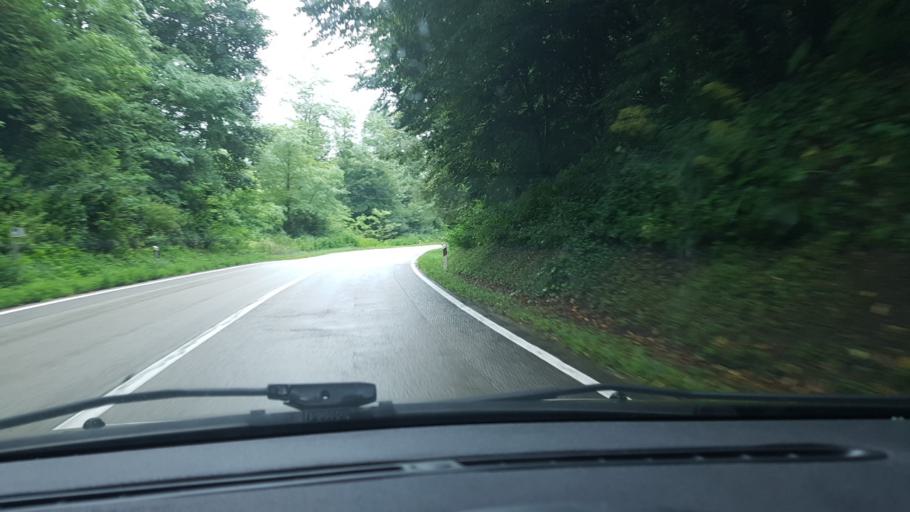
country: HR
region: Karlovacka
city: Ozalj
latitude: 45.4456
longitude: 15.3444
